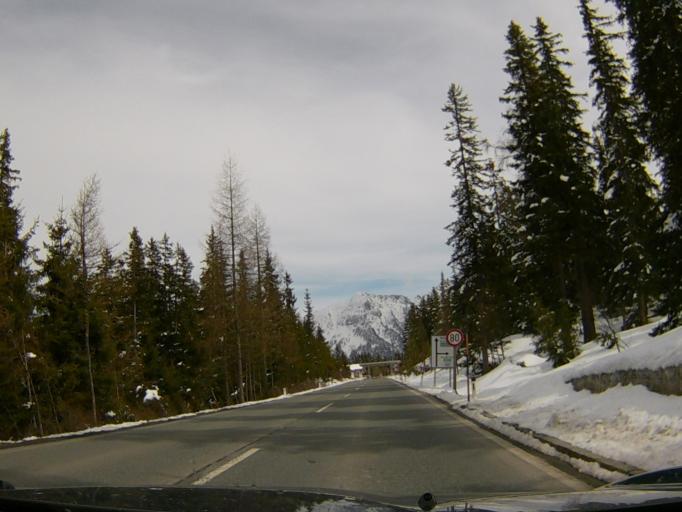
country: AT
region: Salzburg
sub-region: Politischer Bezirk Zell am See
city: Krimml
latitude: 47.2385
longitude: 12.1551
